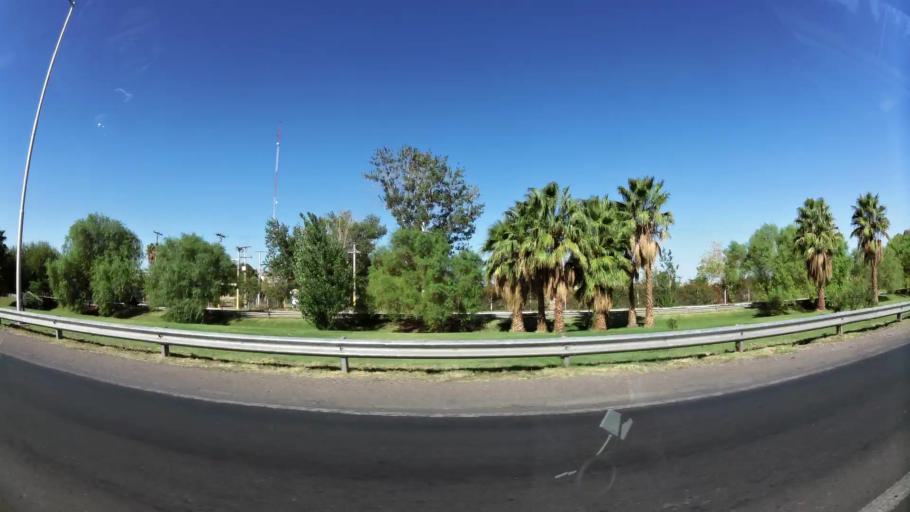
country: AR
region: San Juan
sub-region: Departamento de Santa Lucia
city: Santa Lucia
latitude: -31.5264
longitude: -68.5032
